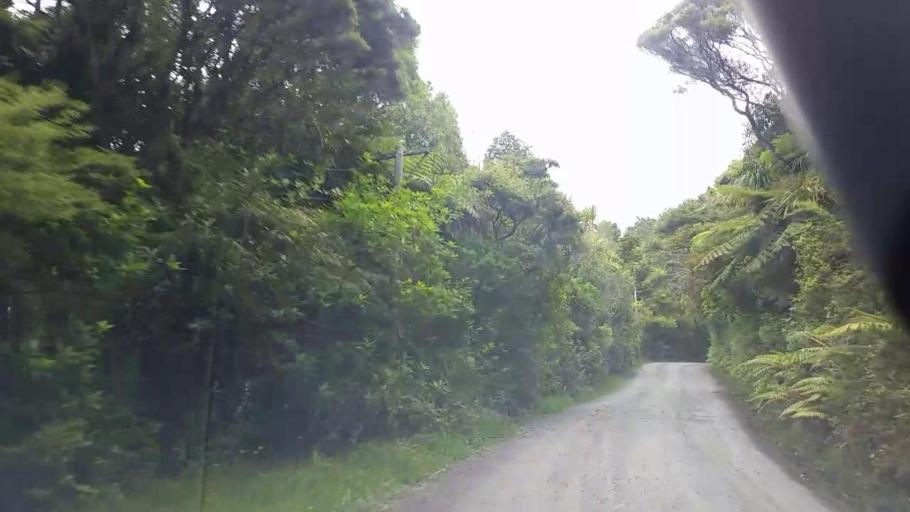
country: NZ
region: Auckland
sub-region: Auckland
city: Titirangi
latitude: -37.0233
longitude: 174.5348
